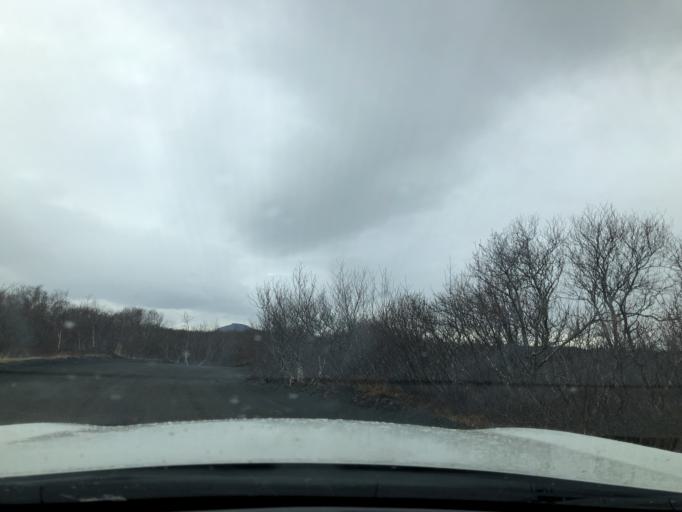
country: IS
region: Northeast
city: Laugar
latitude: 65.6072
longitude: -16.8961
